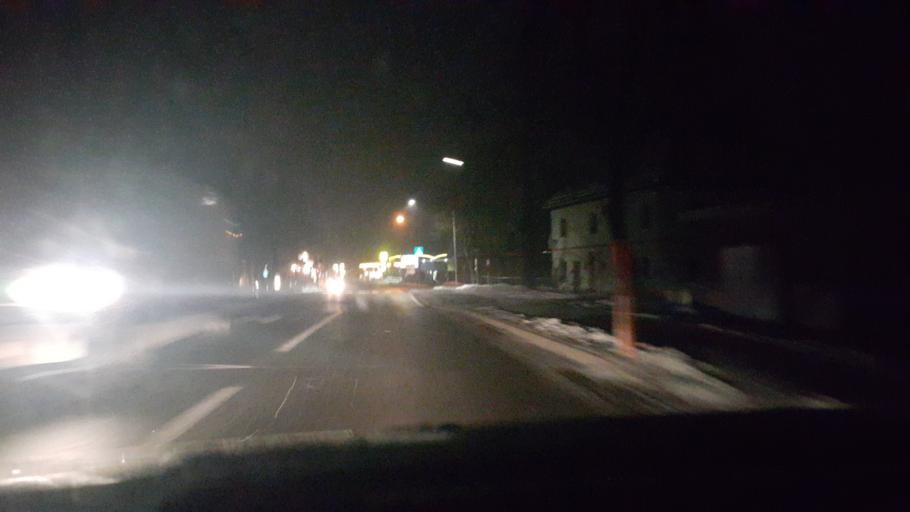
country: AT
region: Carinthia
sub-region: Politischer Bezirk Klagenfurt Land
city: Ebenthal
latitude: 46.6094
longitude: 14.3514
